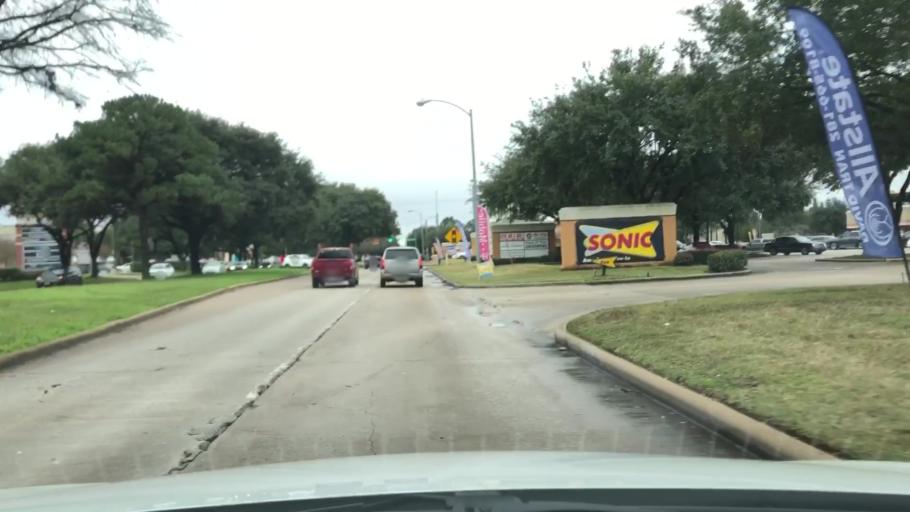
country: US
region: Texas
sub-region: Fort Bend County
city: Cinco Ranch
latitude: 29.7604
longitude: -95.7517
